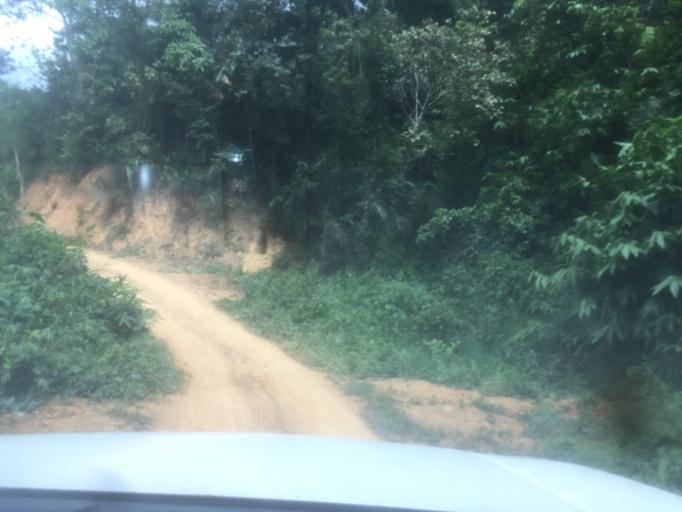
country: LA
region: Phongsali
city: Khoa
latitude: 20.9100
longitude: 102.5566
